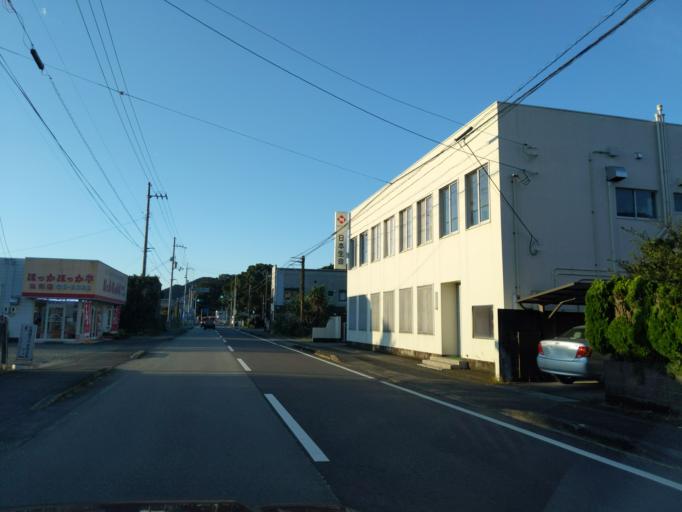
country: JP
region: Kochi
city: Muroto-misakicho
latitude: 33.6078
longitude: 134.3516
